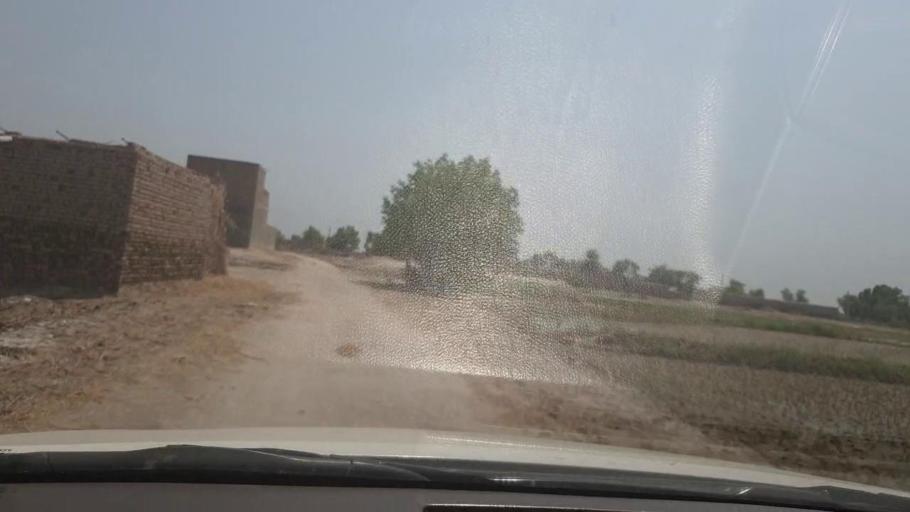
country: PK
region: Sindh
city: Shikarpur
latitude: 28.0415
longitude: 68.5733
